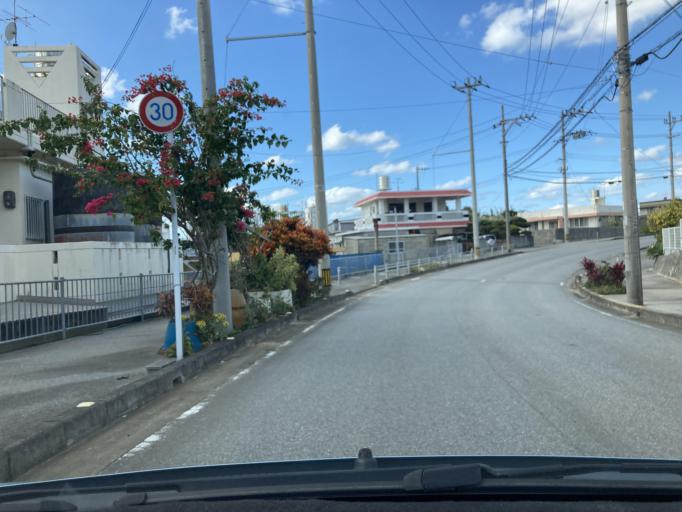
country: JP
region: Okinawa
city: Gushikawa
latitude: 26.3734
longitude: 127.8320
